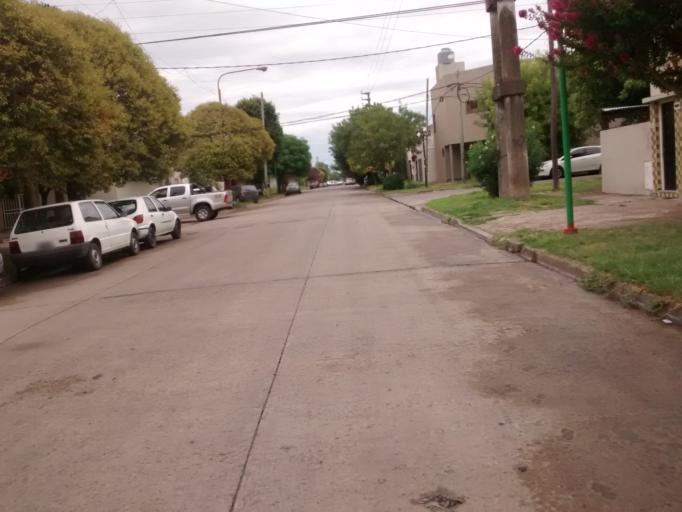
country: AR
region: Buenos Aires
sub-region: Partido de La Plata
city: La Plata
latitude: -34.8961
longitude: -57.9862
